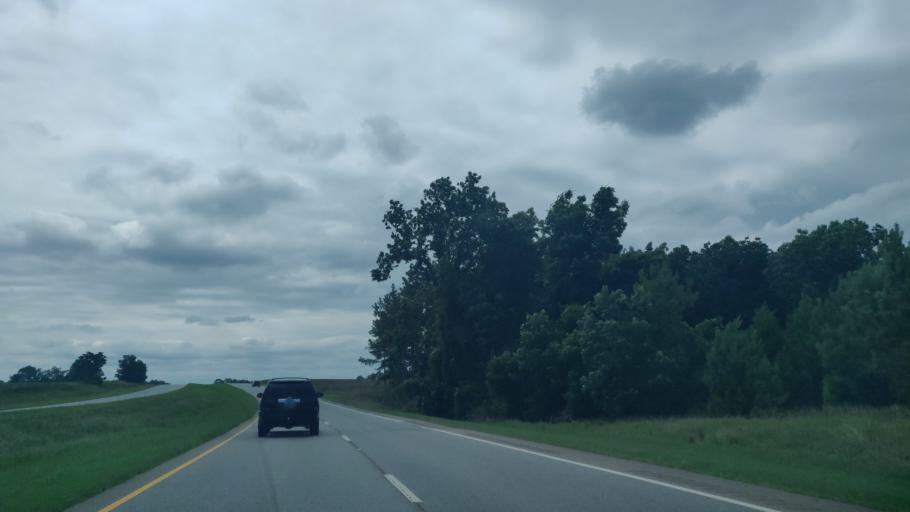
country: US
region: Georgia
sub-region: Terrell County
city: Dawson
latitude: 31.8601
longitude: -84.4825
